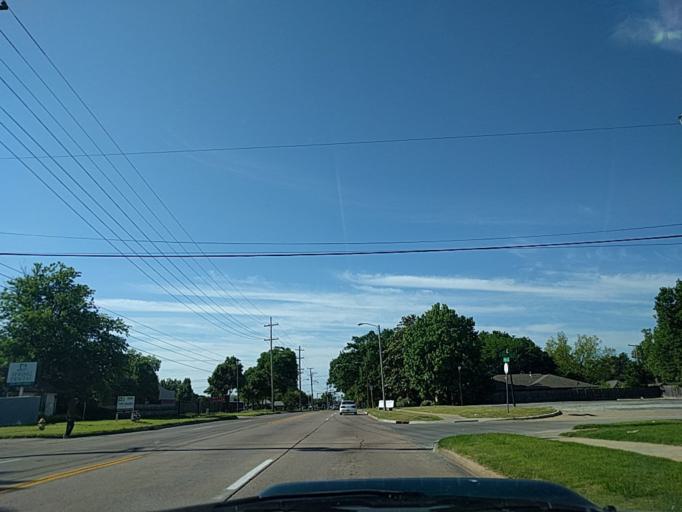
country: US
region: Oklahoma
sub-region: Tulsa County
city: Jenks
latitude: 36.0846
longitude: -95.9758
